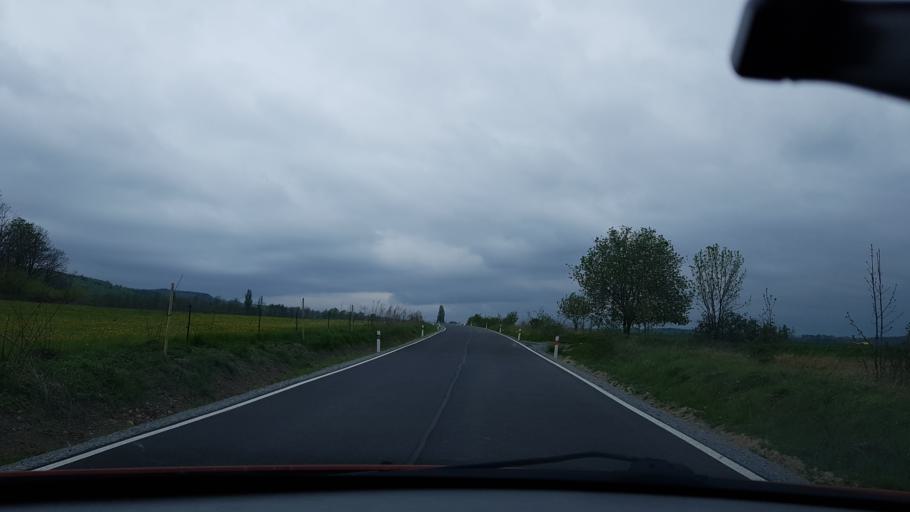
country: PL
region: Opole Voivodeship
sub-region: Powiat nyski
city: Kamienica
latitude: 50.4341
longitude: 16.9455
